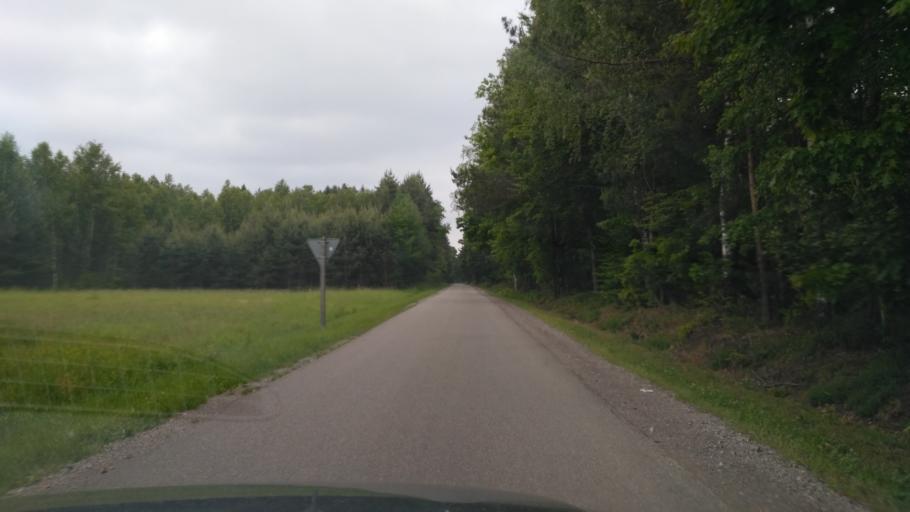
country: PL
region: Subcarpathian Voivodeship
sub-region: Powiat kolbuszowski
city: Niwiska
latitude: 50.2120
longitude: 21.6641
